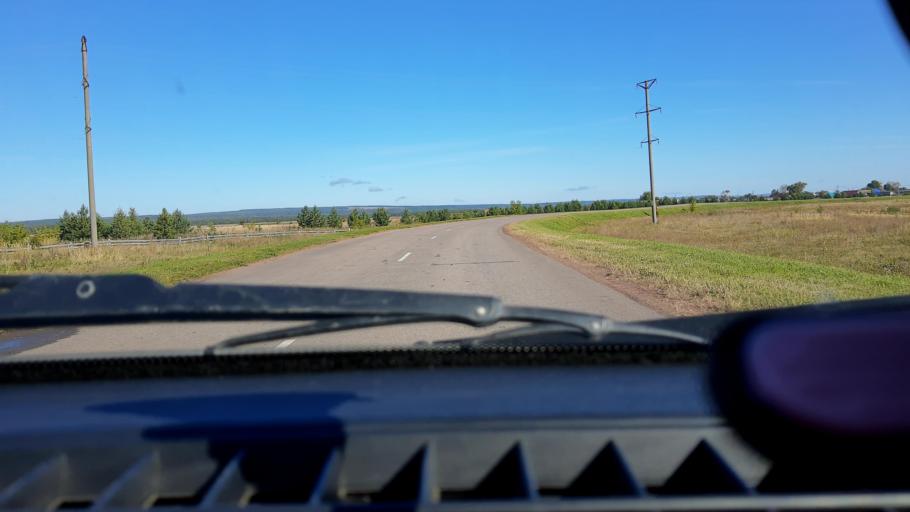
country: RU
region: Bashkortostan
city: Kushnarenkovo
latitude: 55.0861
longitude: 55.4780
